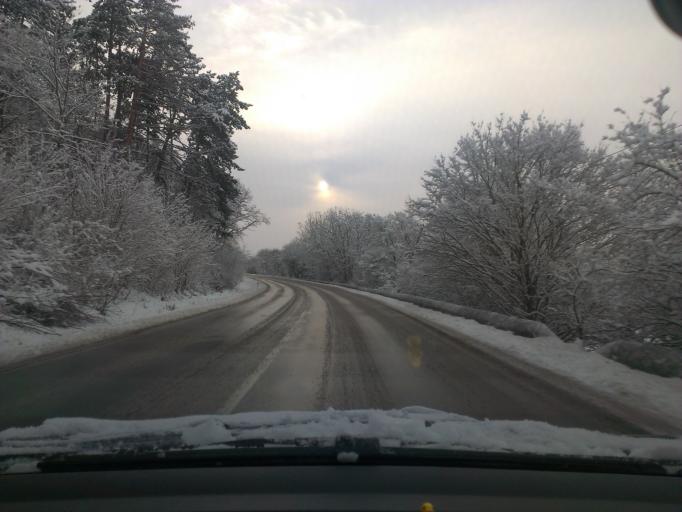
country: SK
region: Trnavsky
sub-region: Okres Trnava
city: Piestany
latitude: 48.5522
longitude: 17.9218
